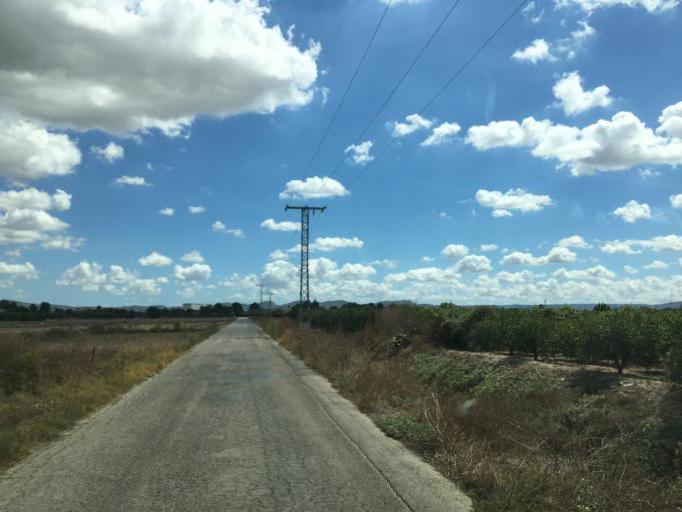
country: ES
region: Murcia
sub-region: Murcia
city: Santomera
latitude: 38.0481
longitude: -1.0457
